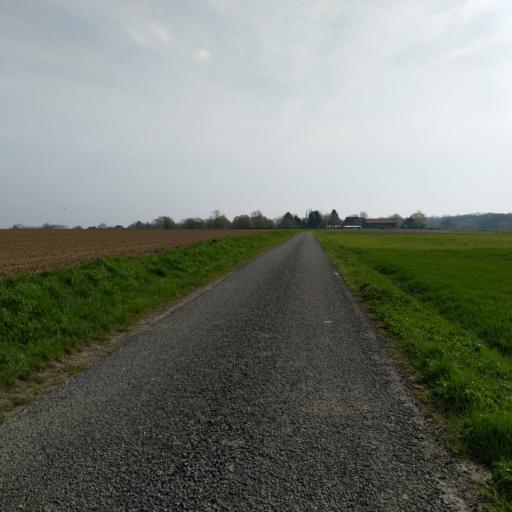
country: FR
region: Nord-Pas-de-Calais
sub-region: Departement du Nord
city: La Longueville
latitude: 50.3286
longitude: 3.8722
